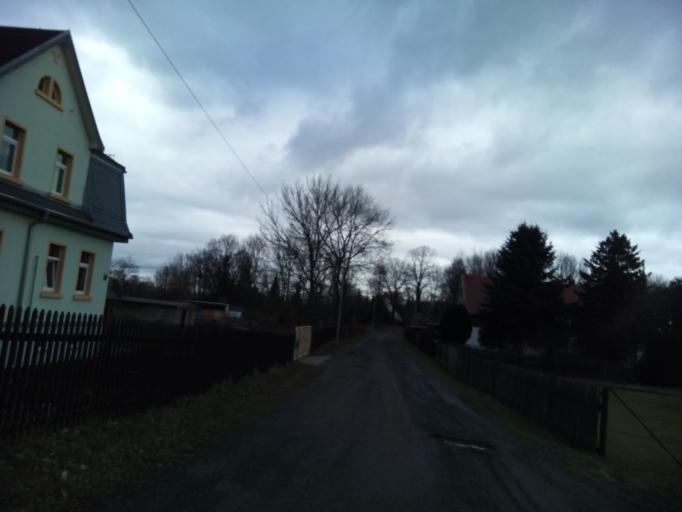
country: DE
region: Saxony
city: Brand-Erbisdorf
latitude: 50.8870
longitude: 13.3330
